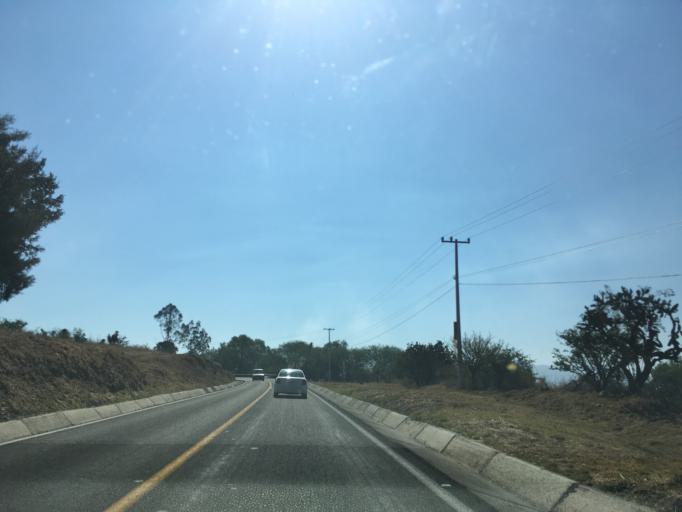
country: MX
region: Michoacan
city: Charo
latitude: 19.7550
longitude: -101.0416
